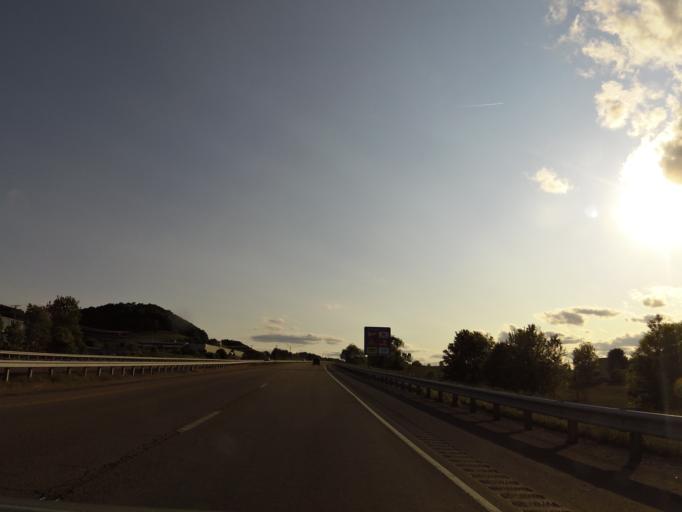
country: US
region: Virginia
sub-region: Russell County
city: Lebanon
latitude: 36.9028
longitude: -82.0471
